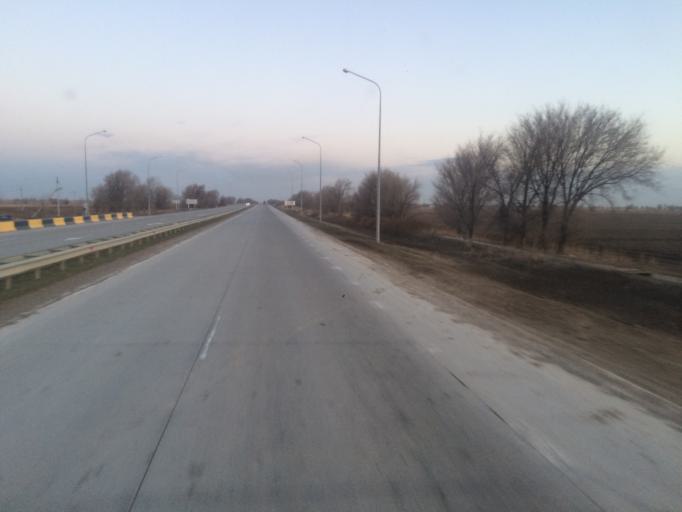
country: KZ
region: Ongtustik Qazaqstan
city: Shayan
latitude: 42.9575
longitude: 68.8930
